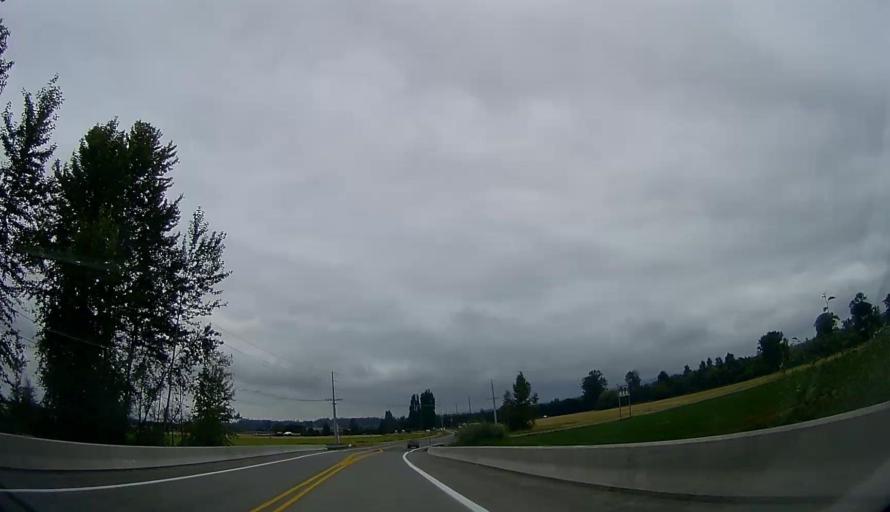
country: US
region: Washington
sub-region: Snohomish County
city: Stanwood
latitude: 48.2118
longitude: -122.3364
